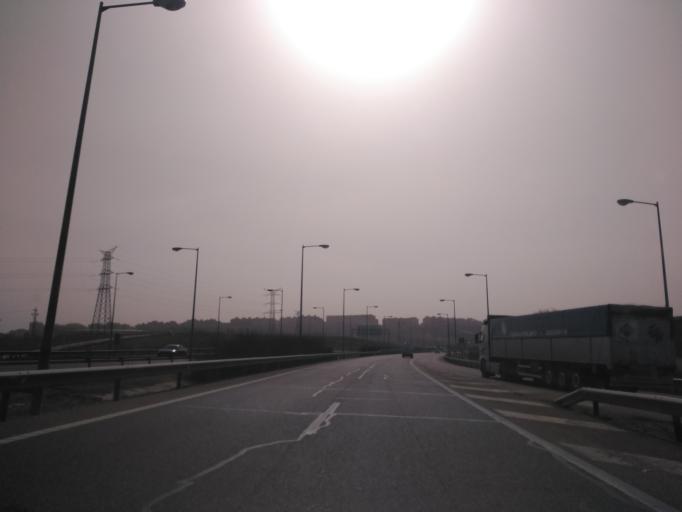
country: ES
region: Castille and Leon
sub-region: Provincia de Valladolid
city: Zaratan
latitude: 41.6510
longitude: -4.7652
